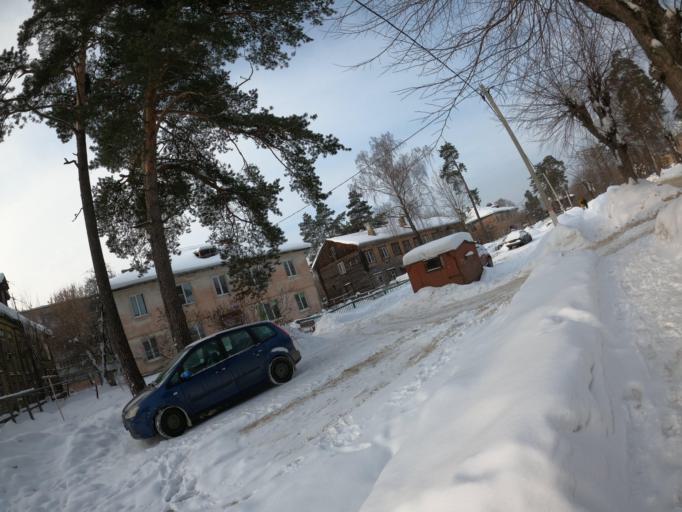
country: RU
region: Moskovskaya
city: Elektrogorsk
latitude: 55.8913
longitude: 38.7711
